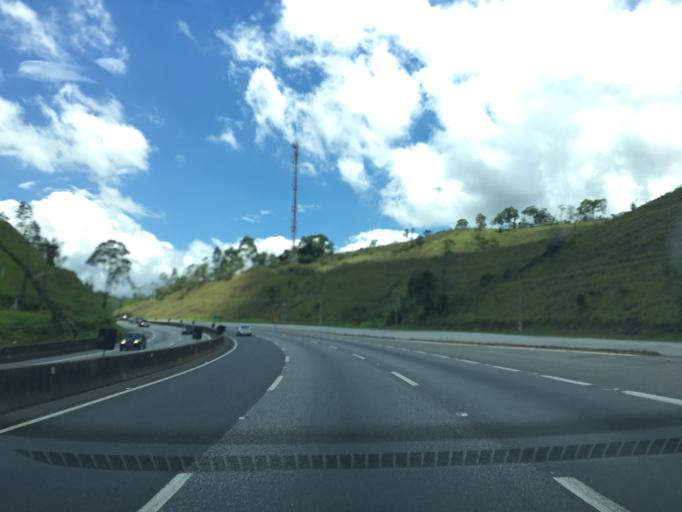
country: BR
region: Sao Paulo
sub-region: Mairipora
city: Mairipora
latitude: -23.2326
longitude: -46.6018
